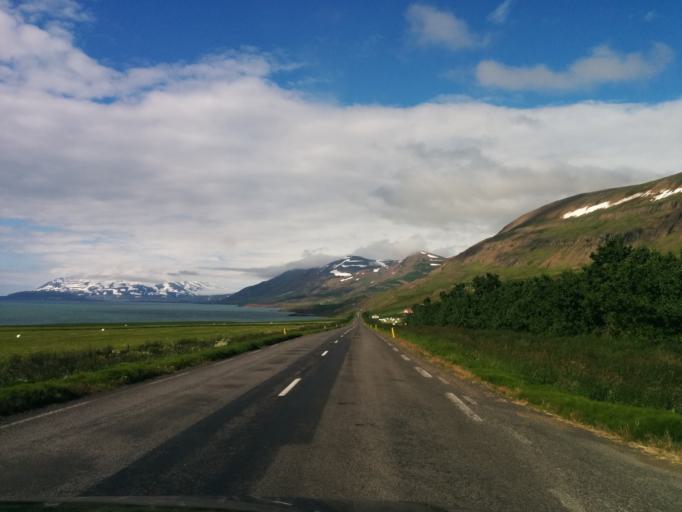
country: IS
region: Northeast
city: Akureyri
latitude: 65.7801
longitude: -18.0663
